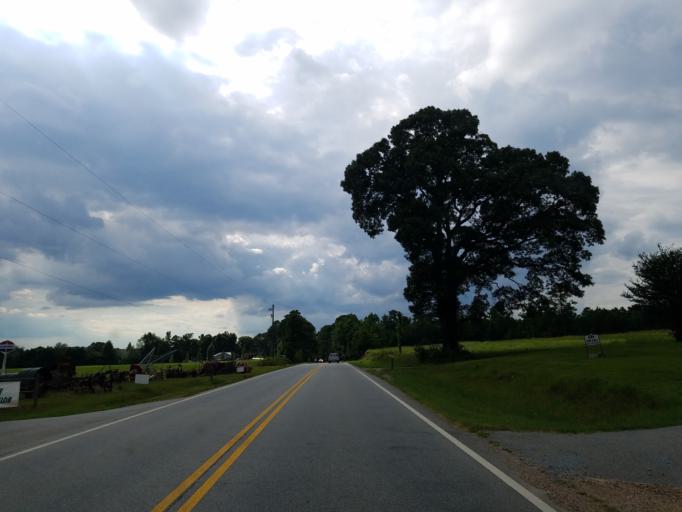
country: US
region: Georgia
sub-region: Floyd County
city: Shannon
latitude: 34.3731
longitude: -85.1009
